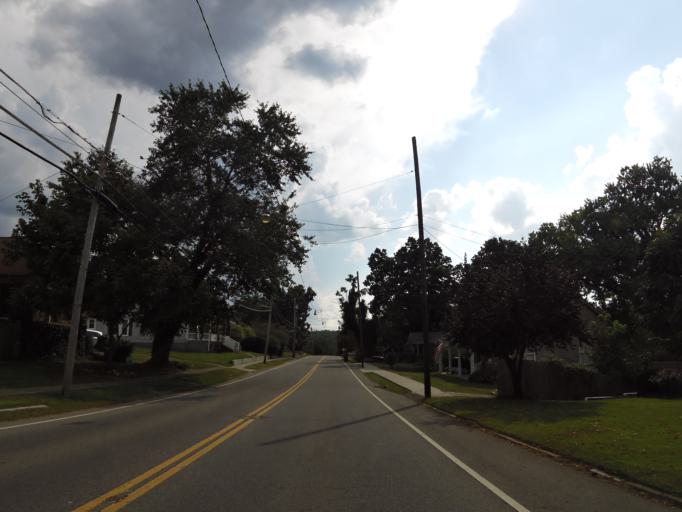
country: US
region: Tennessee
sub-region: Dickson County
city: Dickson
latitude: 36.0710
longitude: -87.3937
